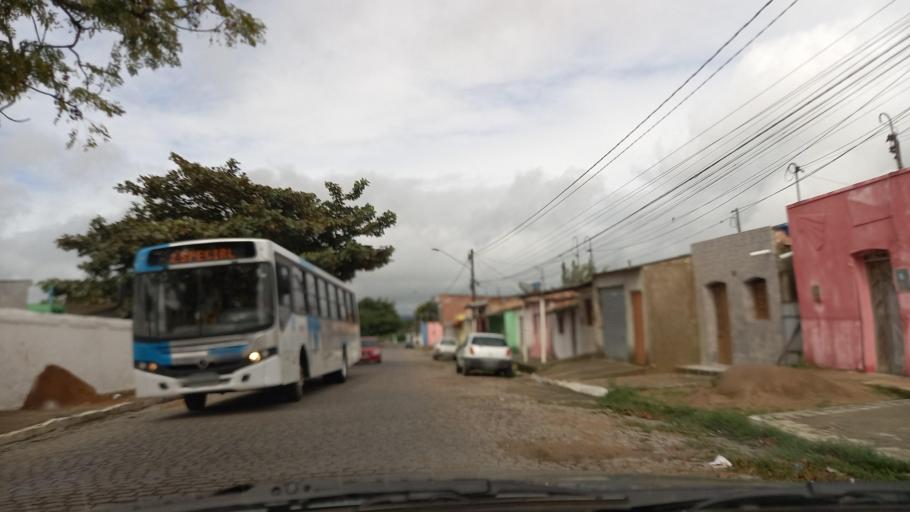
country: BR
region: Pernambuco
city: Garanhuns
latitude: -8.9051
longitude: -36.4968
